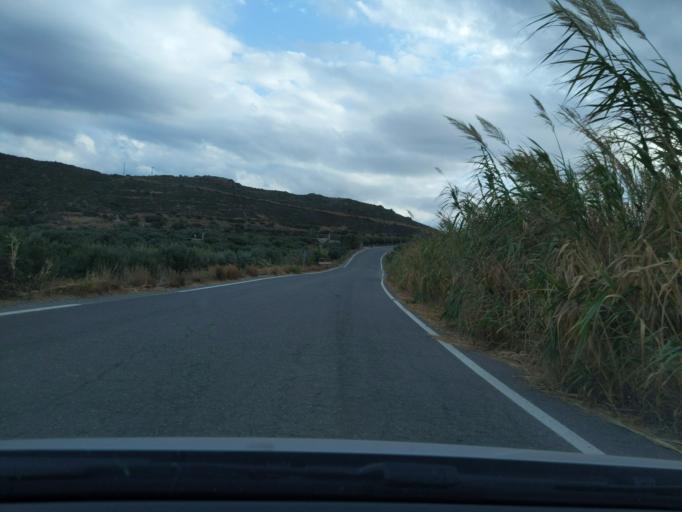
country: GR
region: Crete
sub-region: Nomos Lasithiou
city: Palekastro
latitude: 35.2230
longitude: 26.2589
